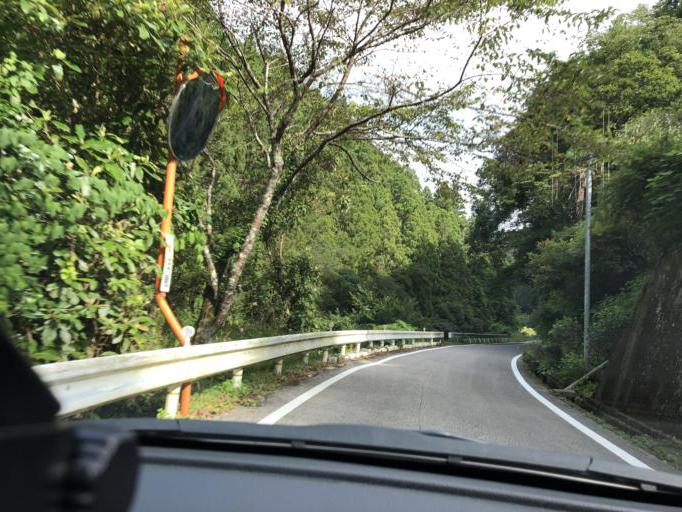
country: JP
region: Kochi
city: Kochi-shi
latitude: 33.6157
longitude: 133.4972
